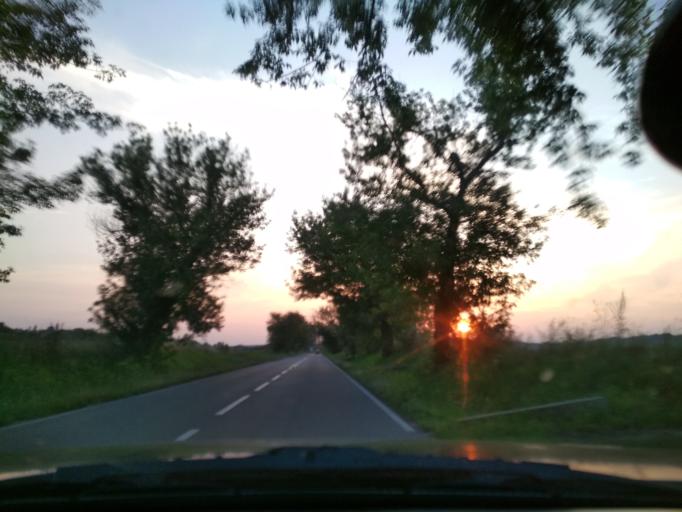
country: PL
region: Lesser Poland Voivodeship
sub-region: Powiat olkuski
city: Wolbrom
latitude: 50.4680
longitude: 19.7590
